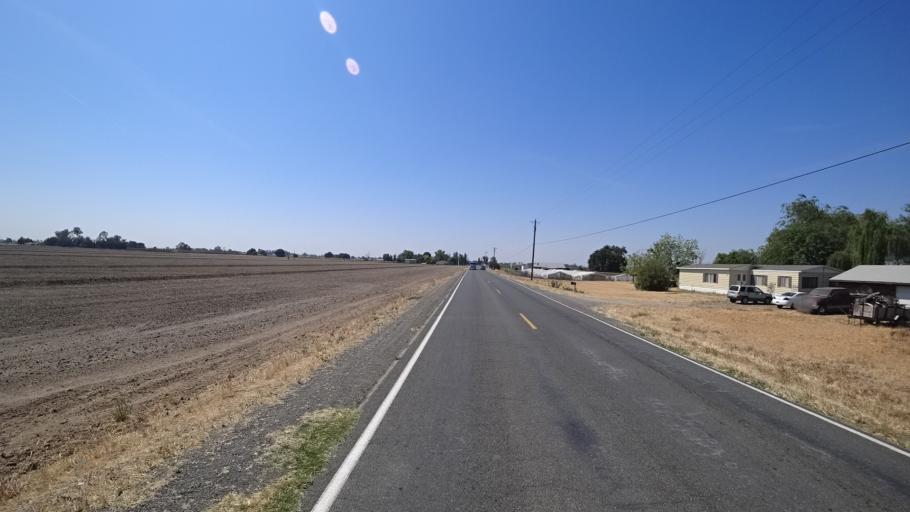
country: US
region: California
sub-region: Fresno County
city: Riverdale
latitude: 36.3782
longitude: -119.8512
